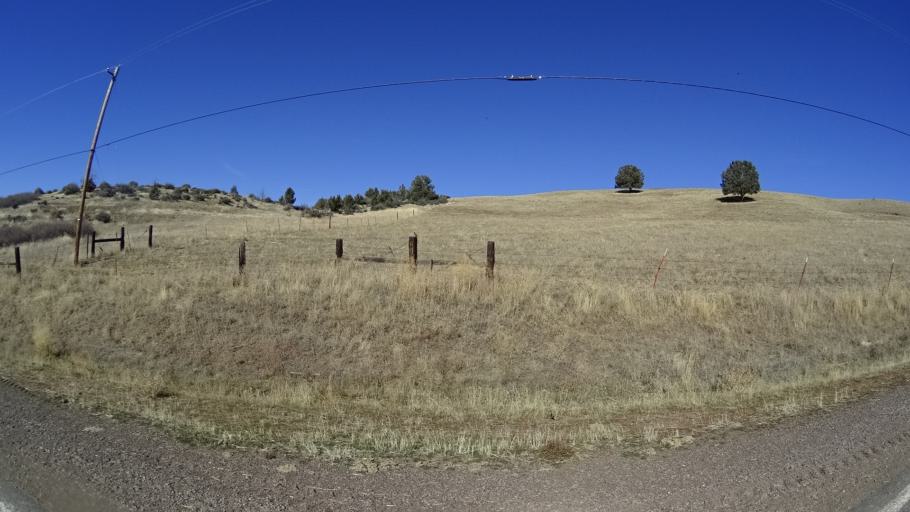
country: US
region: California
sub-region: Siskiyou County
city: Montague
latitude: 41.8083
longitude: -122.3812
